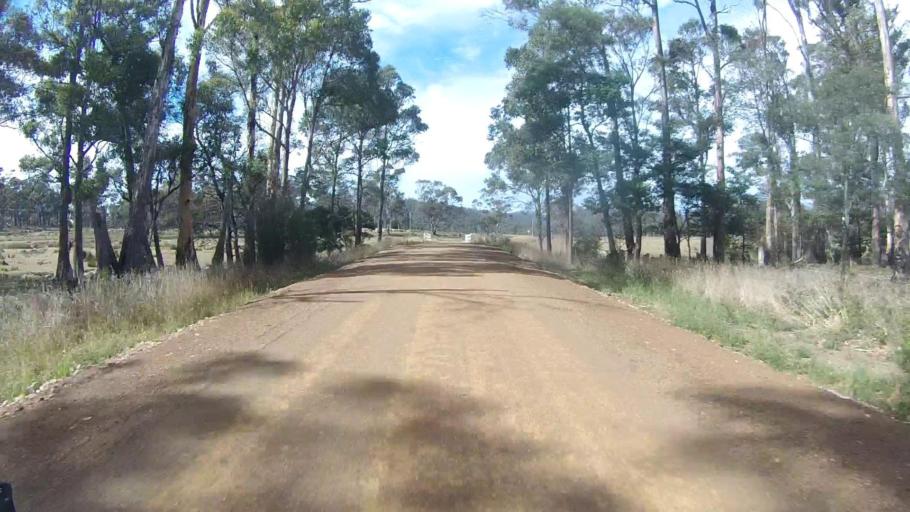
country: AU
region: Tasmania
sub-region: Sorell
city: Sorell
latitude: -42.6420
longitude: 147.9006
